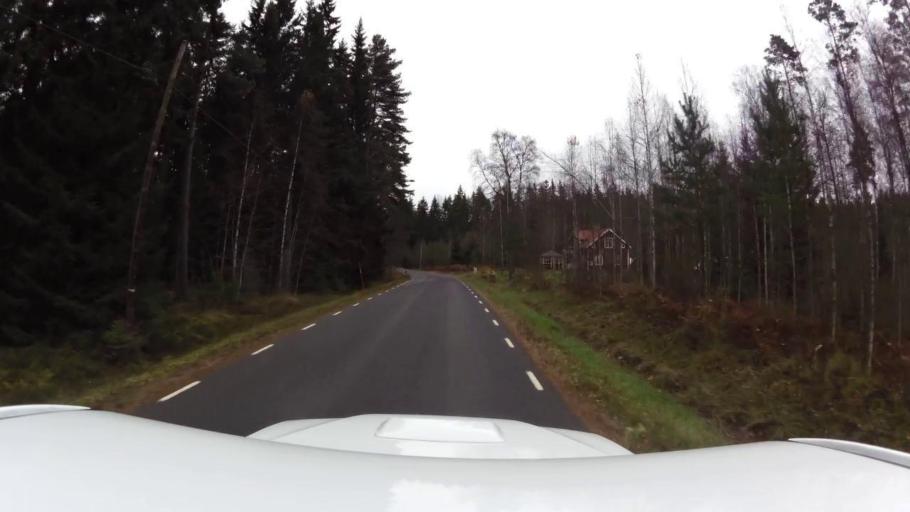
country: SE
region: OEstergoetland
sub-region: Kinda Kommun
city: Kisa
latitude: 58.1364
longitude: 15.4529
